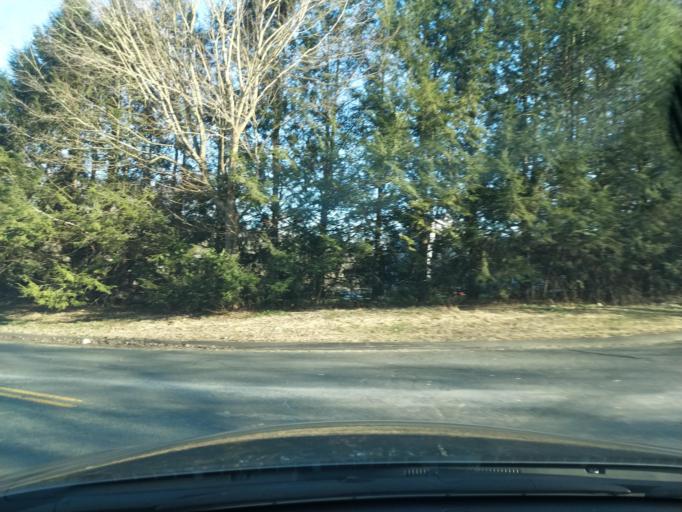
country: US
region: Connecticut
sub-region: Fairfield County
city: Newtown
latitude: 41.3601
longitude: -73.2839
